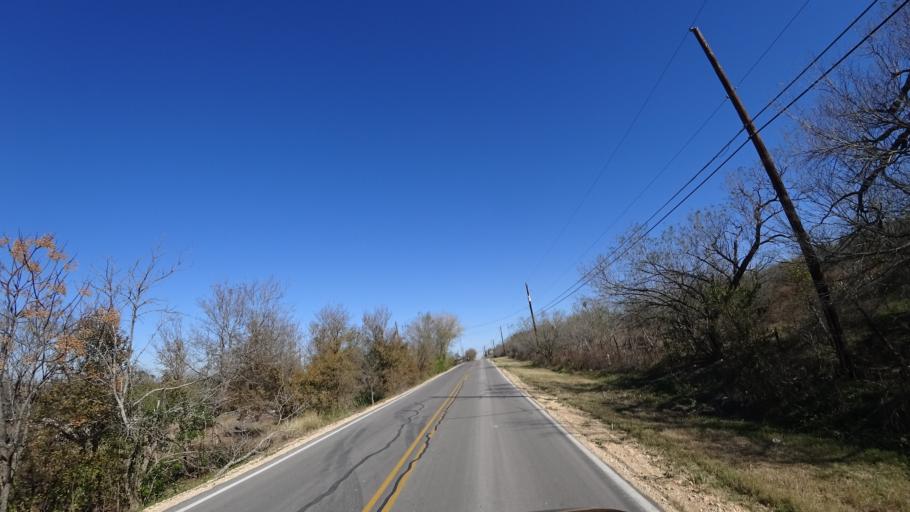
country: US
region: Texas
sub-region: Travis County
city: Garfield
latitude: 30.1238
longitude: -97.6429
